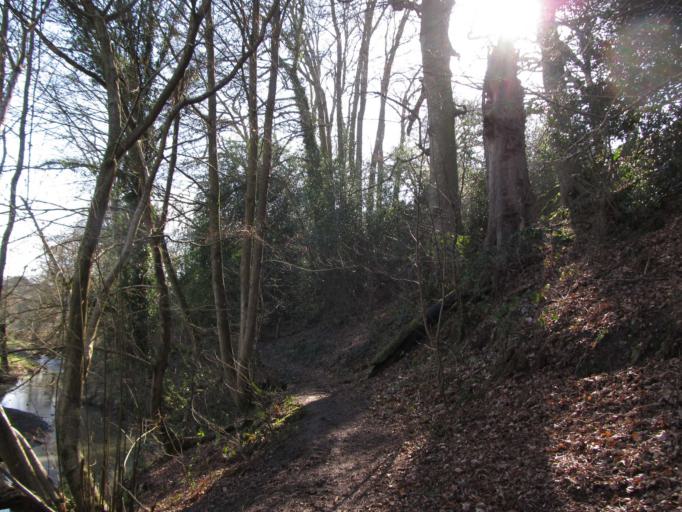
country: GB
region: England
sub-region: West Sussex
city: Petworth
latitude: 50.9807
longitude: -0.5992
